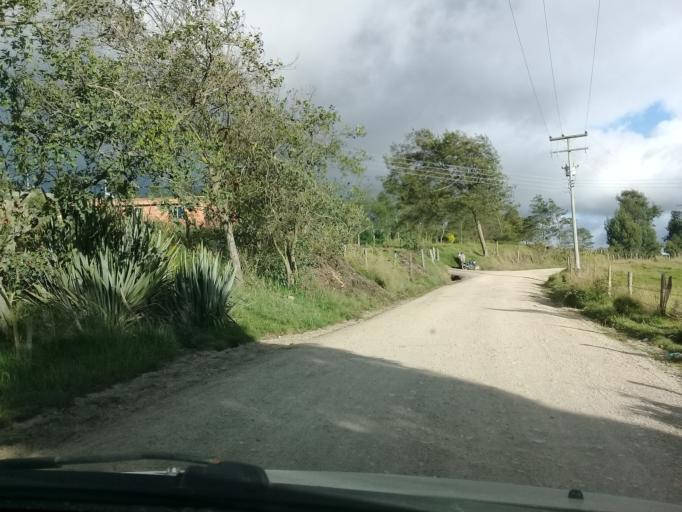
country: CO
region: Cundinamarca
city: Villapinzon
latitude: 5.2404
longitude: -73.6537
